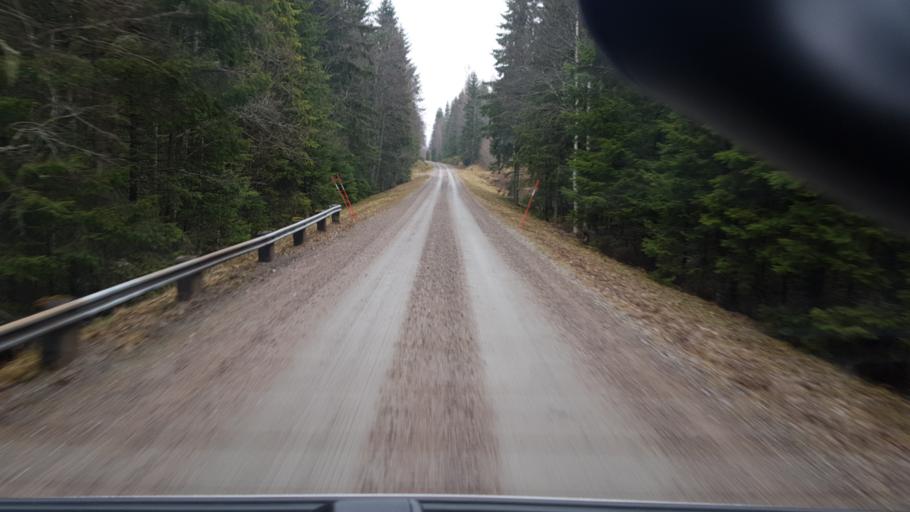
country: SE
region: Vaermland
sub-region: Eda Kommun
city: Charlottenberg
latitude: 59.9912
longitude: 12.5048
